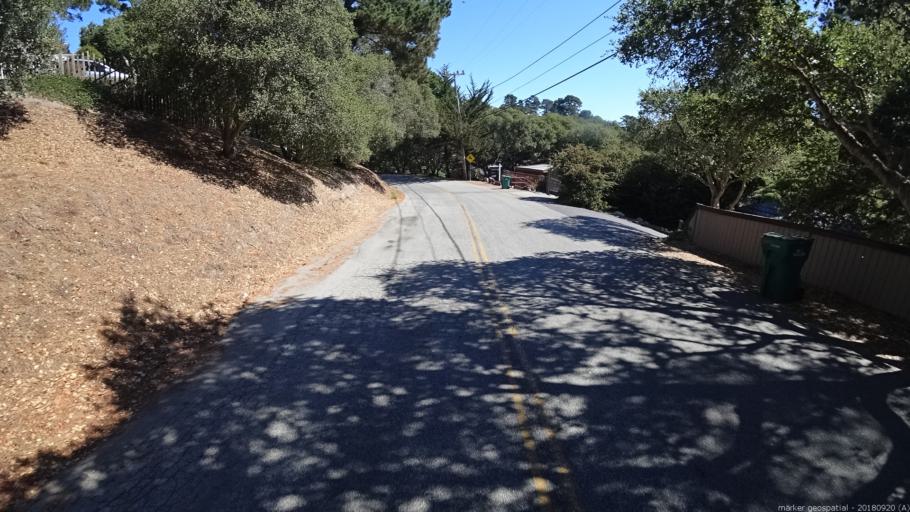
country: US
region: California
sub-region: Monterey County
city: Carmel-by-the-Sea
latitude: 36.5536
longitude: -121.9069
